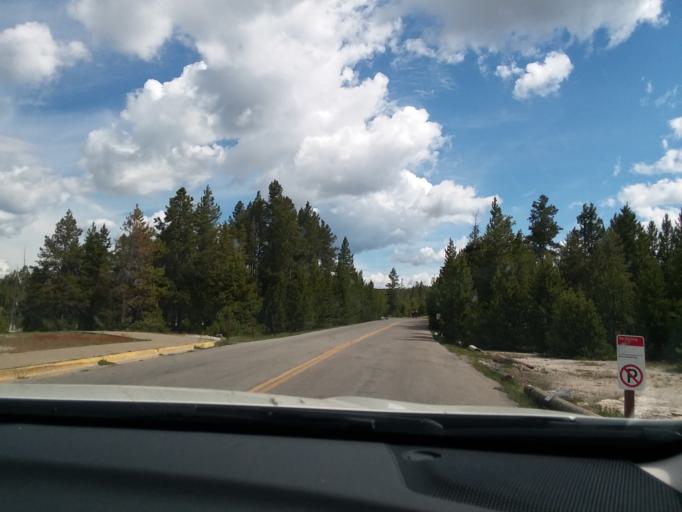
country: US
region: Montana
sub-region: Gallatin County
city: West Yellowstone
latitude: 44.4626
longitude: -110.8531
